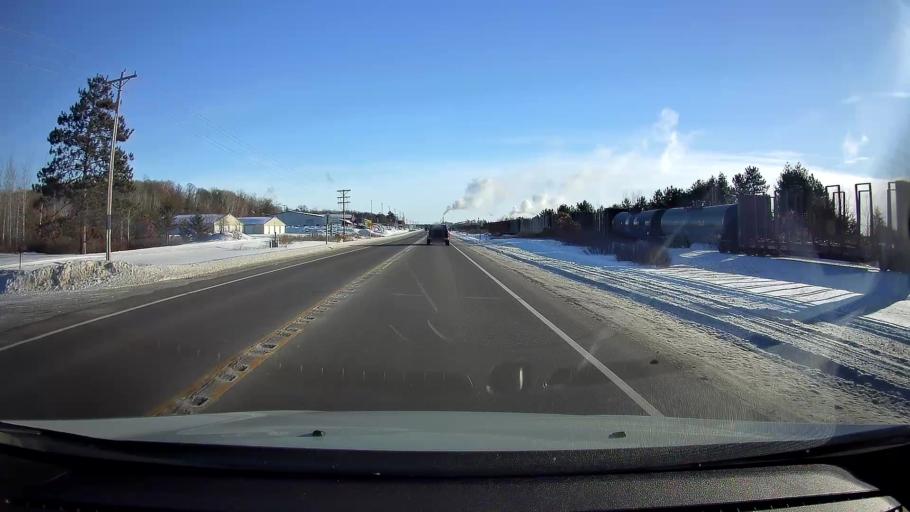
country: US
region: Wisconsin
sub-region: Sawyer County
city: Hayward
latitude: 45.9844
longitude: -91.5394
